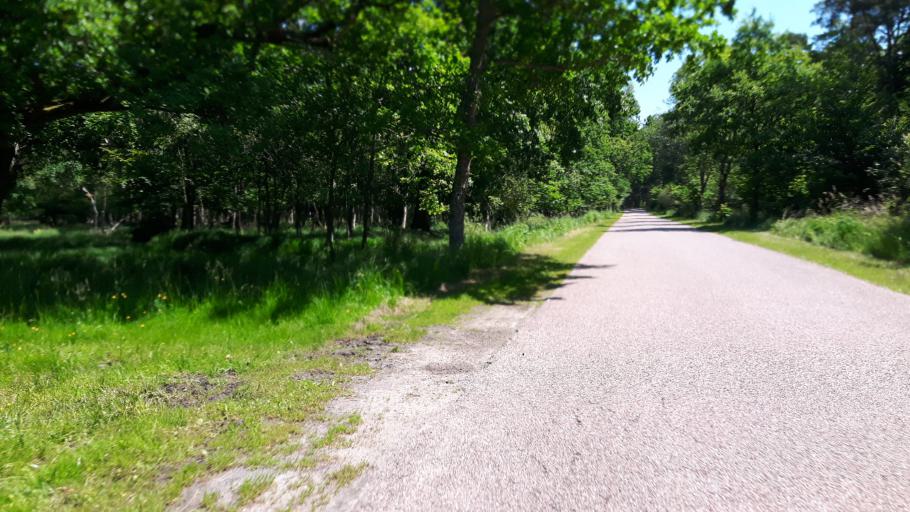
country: PL
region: Pomeranian Voivodeship
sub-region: Powiat slupski
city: Glowczyce
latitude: 54.6820
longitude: 17.3149
